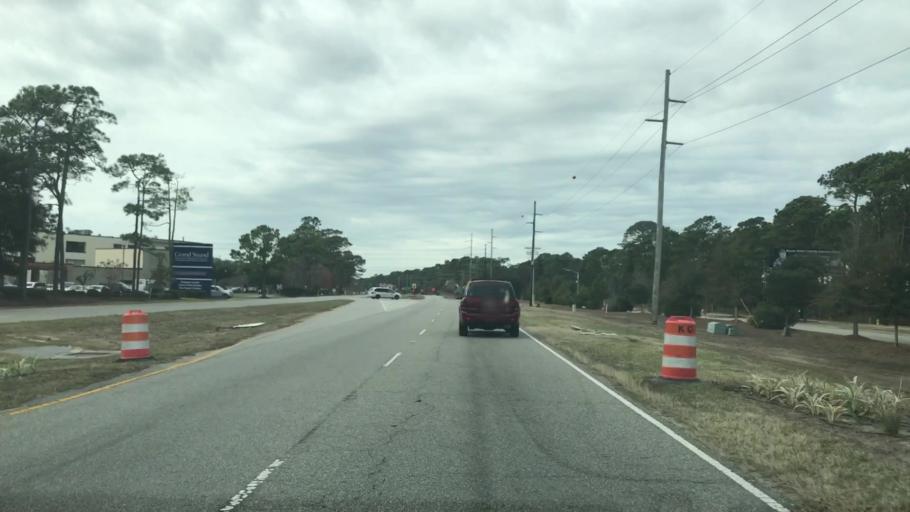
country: US
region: South Carolina
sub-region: Horry County
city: Myrtle Beach
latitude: 33.7603
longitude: -78.8195
